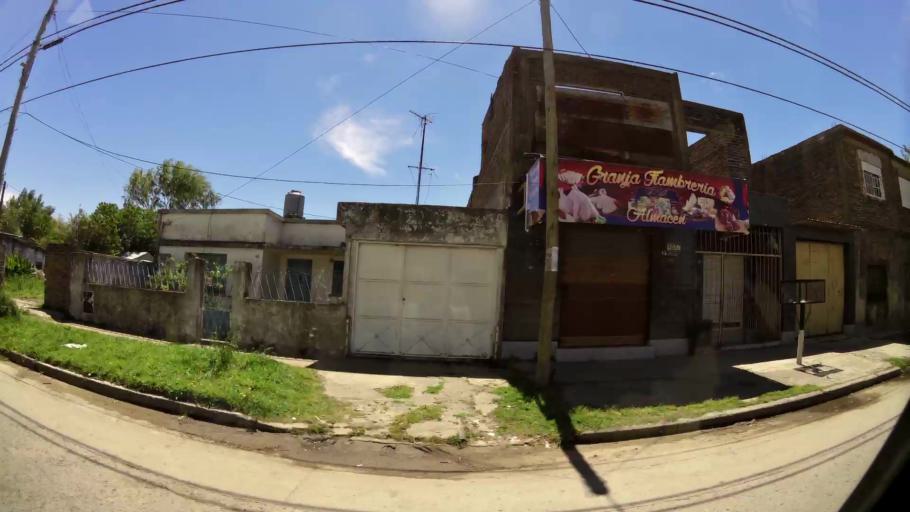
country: AR
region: Buenos Aires
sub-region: Partido de Quilmes
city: Quilmes
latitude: -34.7384
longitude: -58.3120
